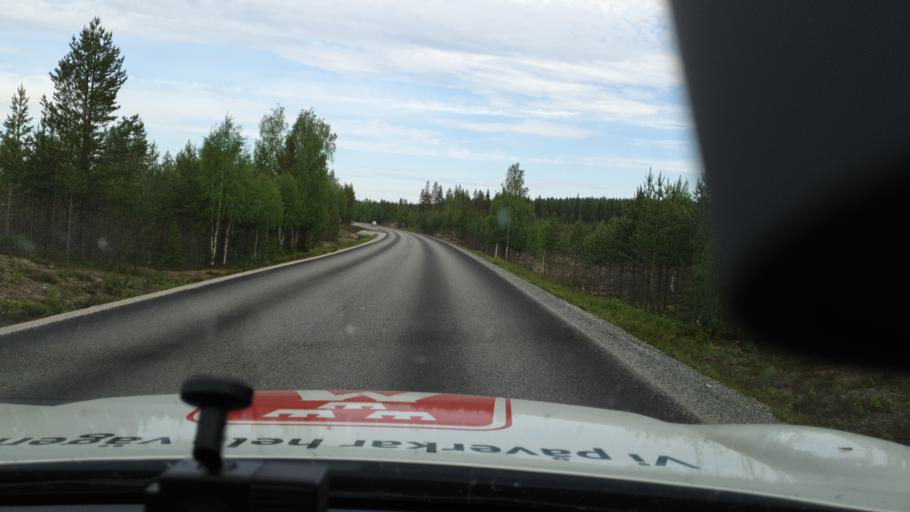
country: SE
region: Vaesterbotten
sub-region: Mala Kommun
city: Mala
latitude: 64.9670
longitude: 18.5814
